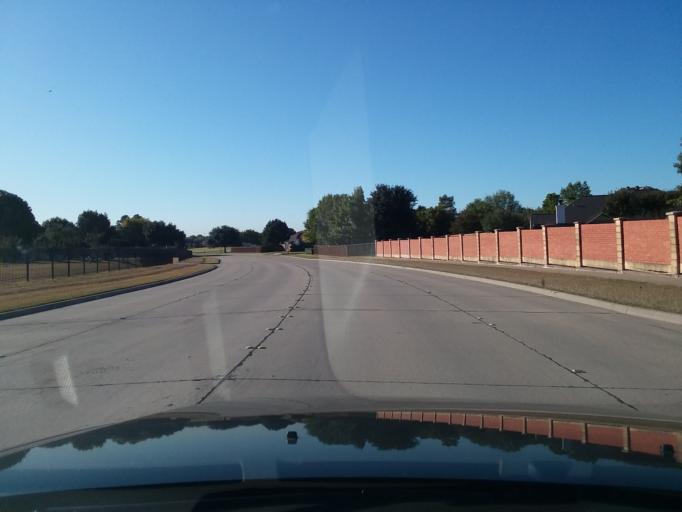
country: US
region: Texas
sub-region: Denton County
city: Highland Village
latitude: 33.0625
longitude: -97.0277
